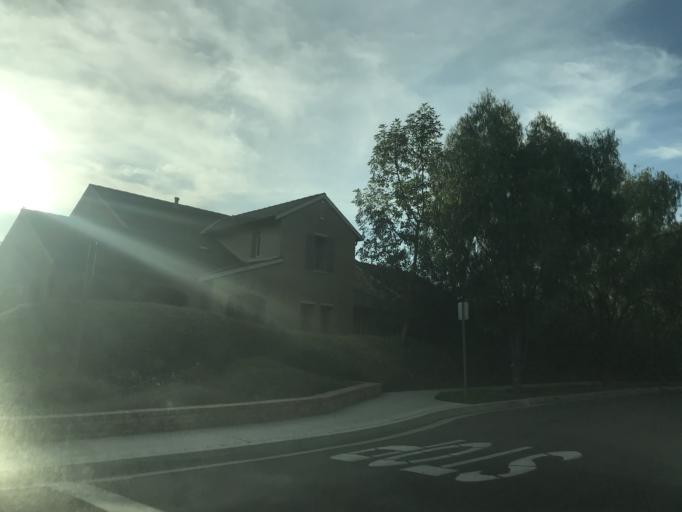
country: US
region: California
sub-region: Orange County
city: North Tustin
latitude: 33.7031
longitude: -117.7483
